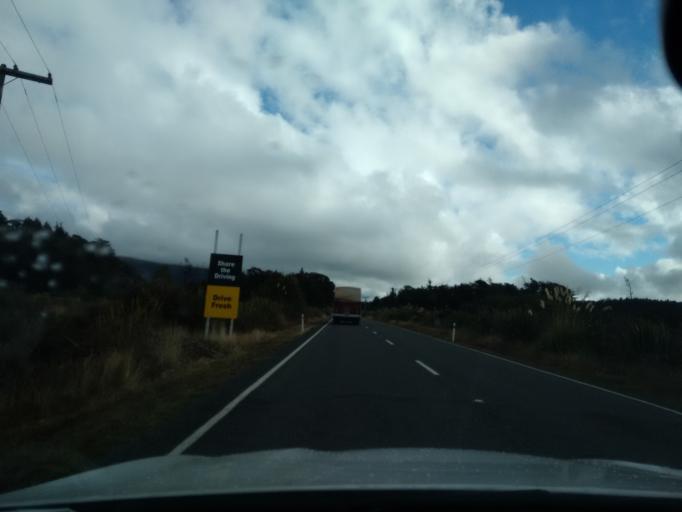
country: NZ
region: Manawatu-Wanganui
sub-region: Ruapehu District
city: Waiouru
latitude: -39.1697
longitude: 175.4800
